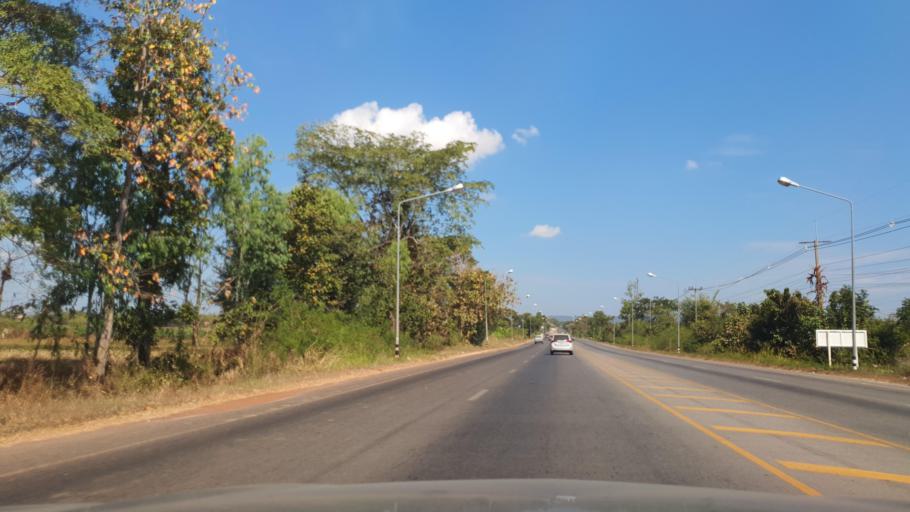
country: TH
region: Kalasin
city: Somdet
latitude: 16.7380
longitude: 103.7682
